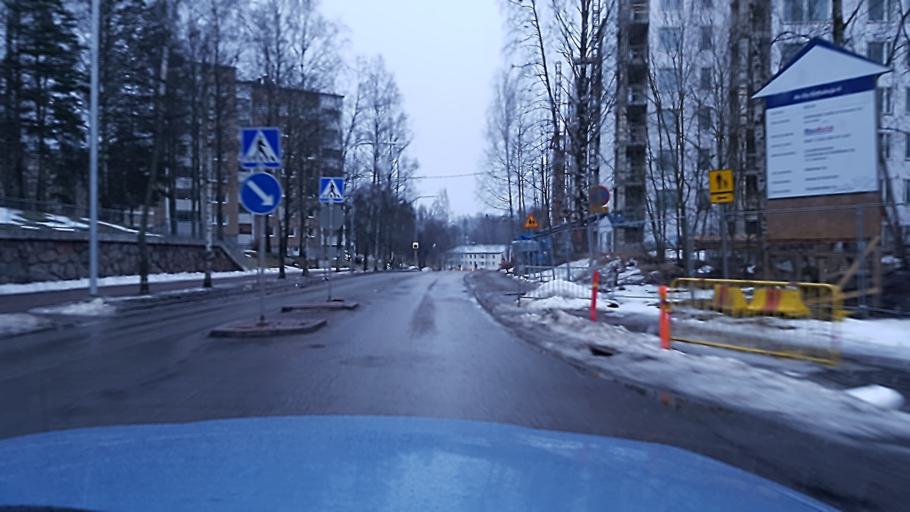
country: FI
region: Uusimaa
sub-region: Helsinki
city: Vantaa
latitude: 60.2091
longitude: 25.0382
